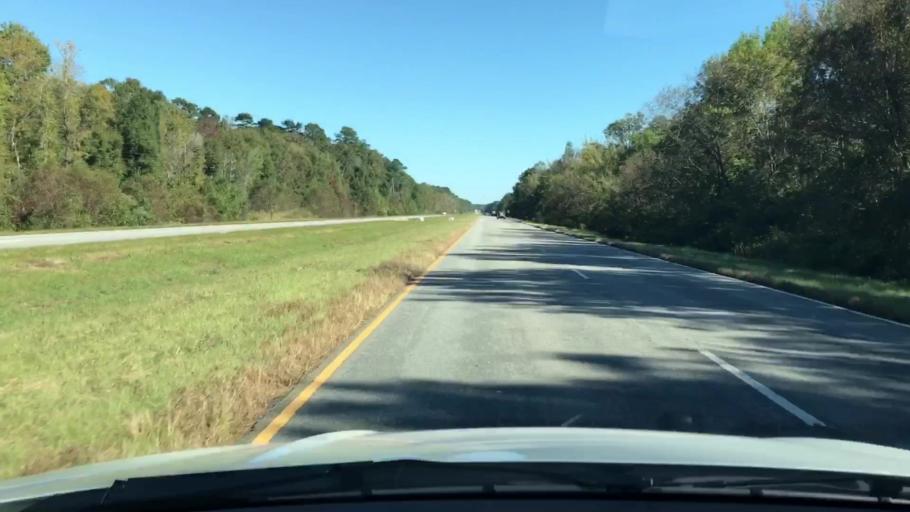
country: US
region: South Carolina
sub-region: Charleston County
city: Ravenel
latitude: 32.7619
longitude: -80.4189
